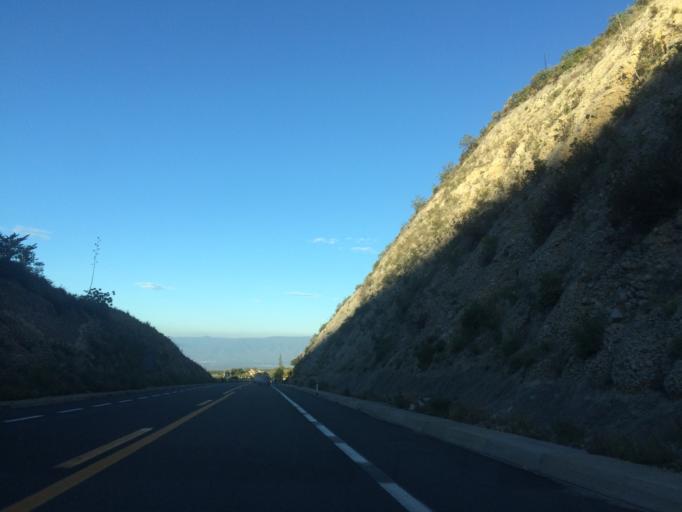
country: MX
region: Puebla
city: Chapuco
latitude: 18.6253
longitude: -97.4635
